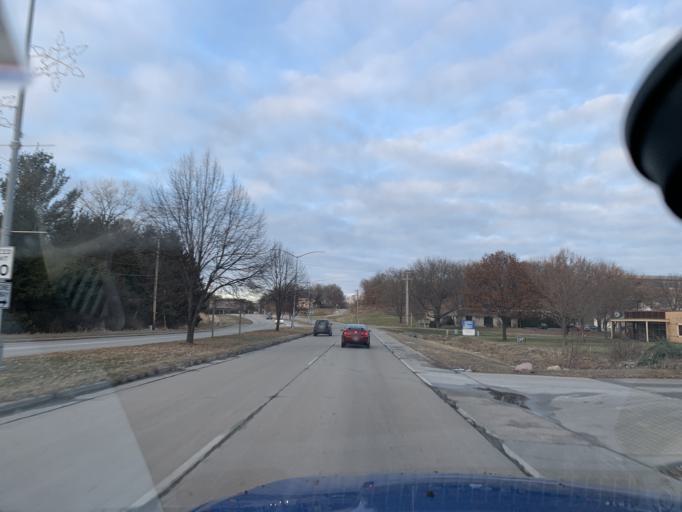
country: US
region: Wisconsin
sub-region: Dane County
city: Fitchburg
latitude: 43.0056
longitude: -89.4276
